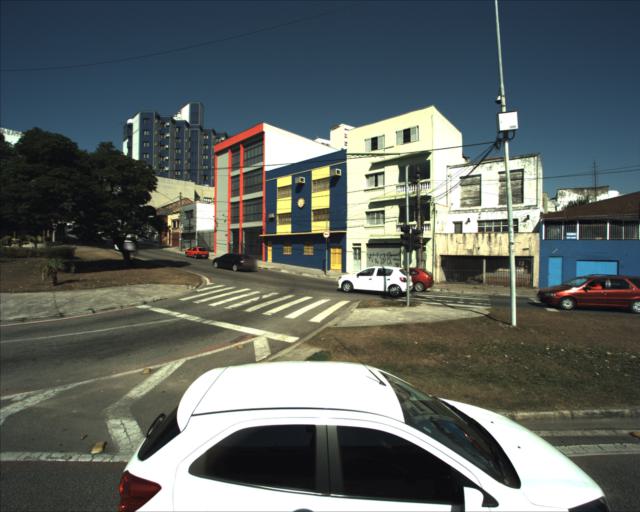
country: BR
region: Sao Paulo
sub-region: Sorocaba
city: Sorocaba
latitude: -23.4962
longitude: -47.4553
